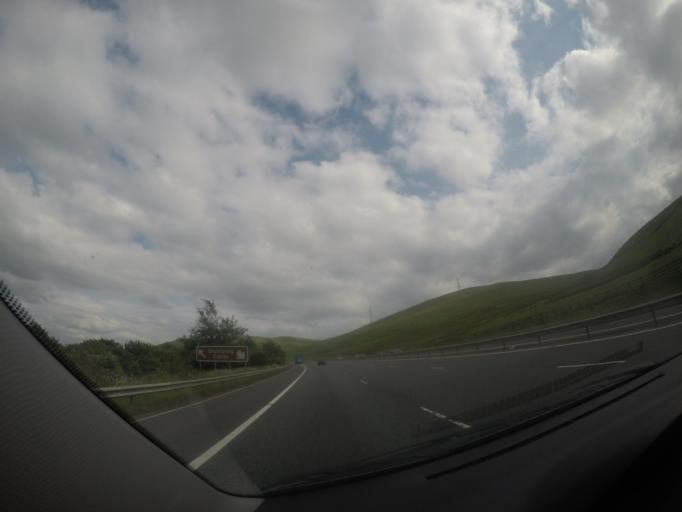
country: GB
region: Scotland
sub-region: South Lanarkshire
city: Douglas
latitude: 55.4721
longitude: -3.6927
